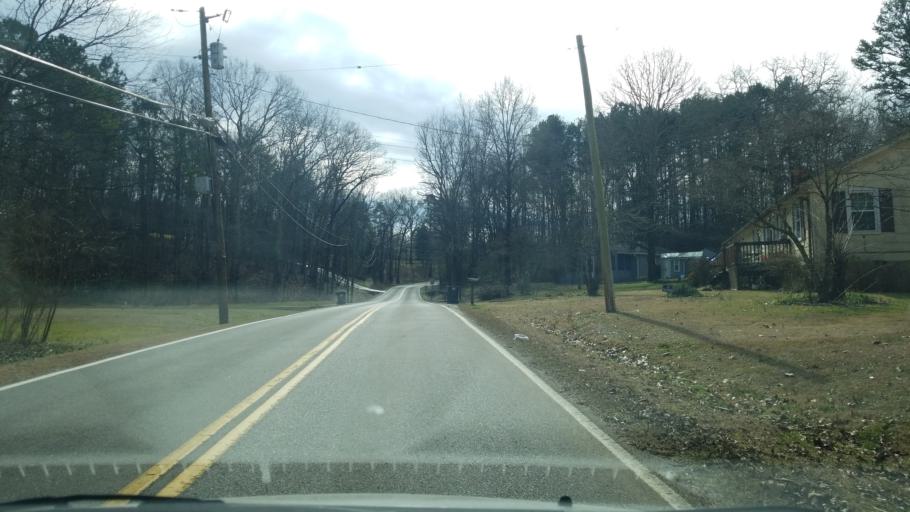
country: US
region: Tennessee
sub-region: Hamilton County
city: Harrison
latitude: 35.0616
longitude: -85.1123
